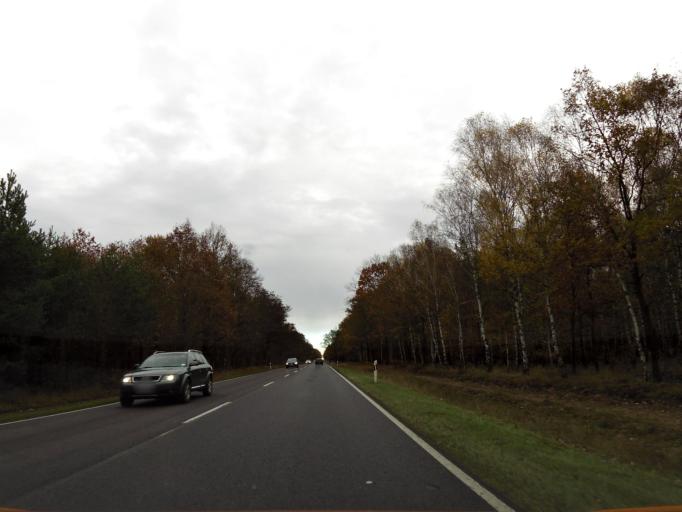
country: DE
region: Saxony-Anhalt
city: Letzlingen
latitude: 52.3985
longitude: 11.4730
